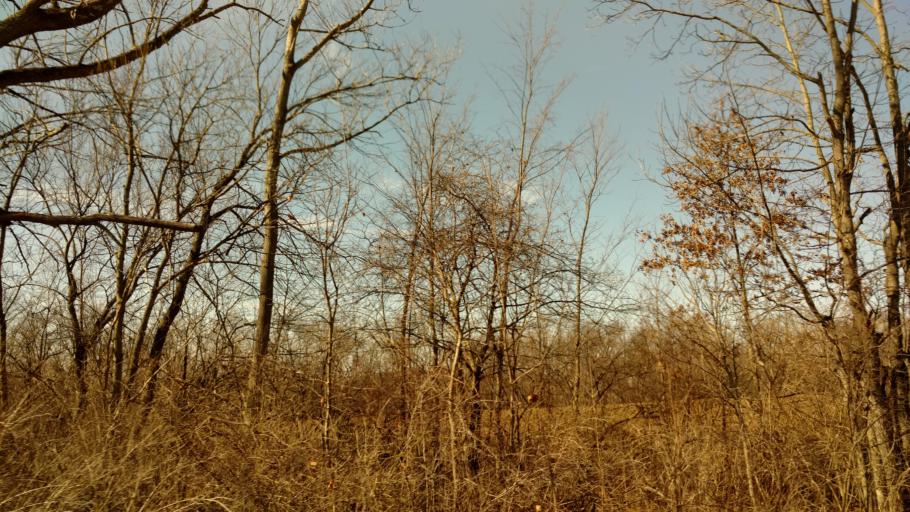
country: US
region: Ohio
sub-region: Marion County
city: Prospect
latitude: 40.4939
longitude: -83.1905
